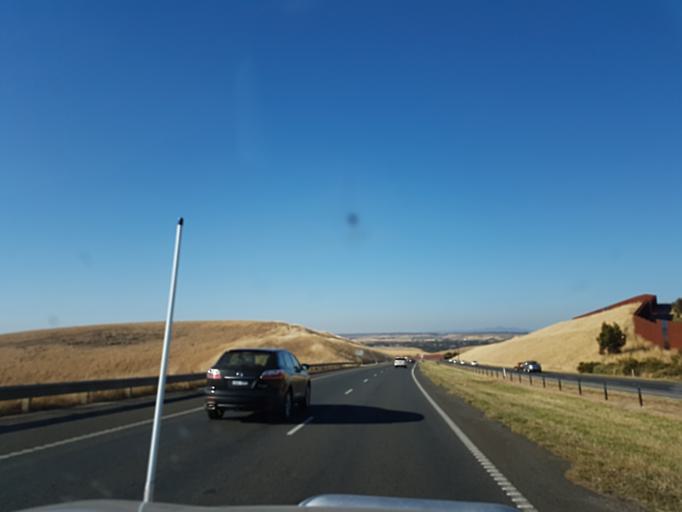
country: AU
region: Victoria
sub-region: Greater Geelong
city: Wandana Heights
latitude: -38.1647
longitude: 144.2922
